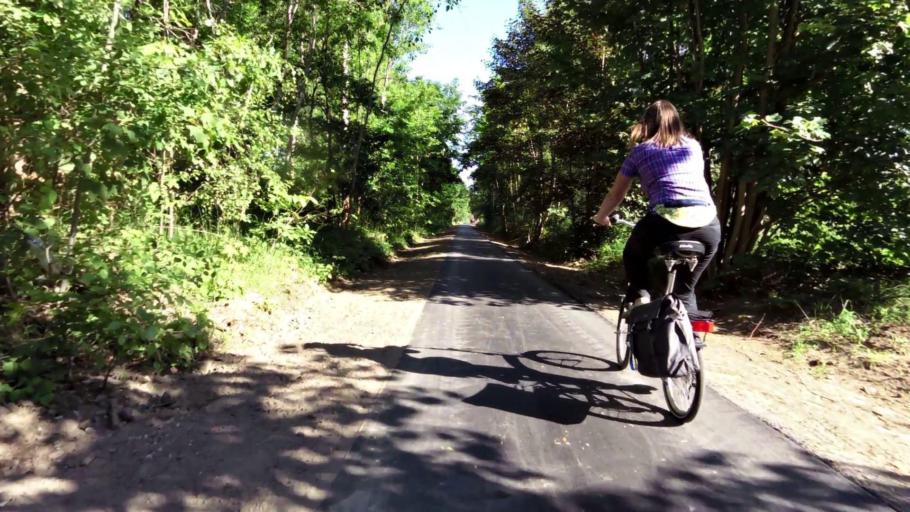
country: PL
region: West Pomeranian Voivodeship
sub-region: Powiat gryfinski
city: Banie
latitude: 53.1967
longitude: 14.6193
